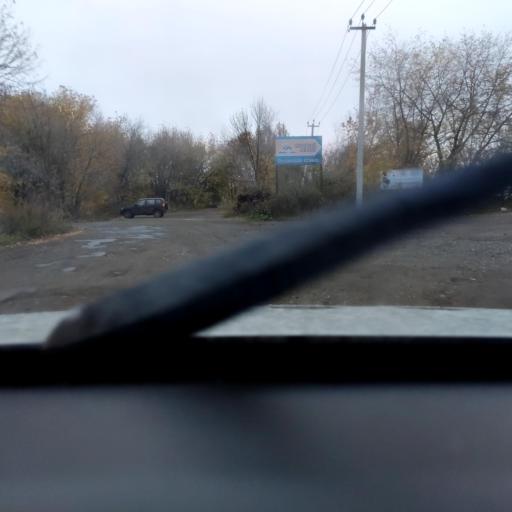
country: RU
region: Perm
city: Perm
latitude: 57.9727
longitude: 56.2102
